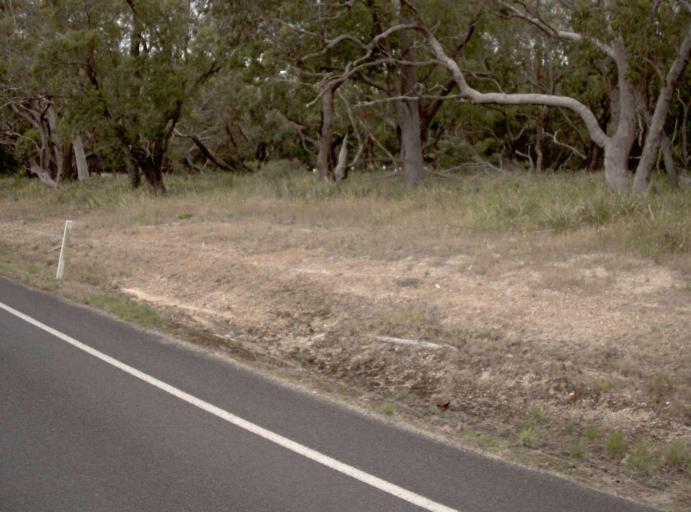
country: AU
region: Victoria
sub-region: Wellington
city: Sale
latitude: -38.2204
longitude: 147.0585
